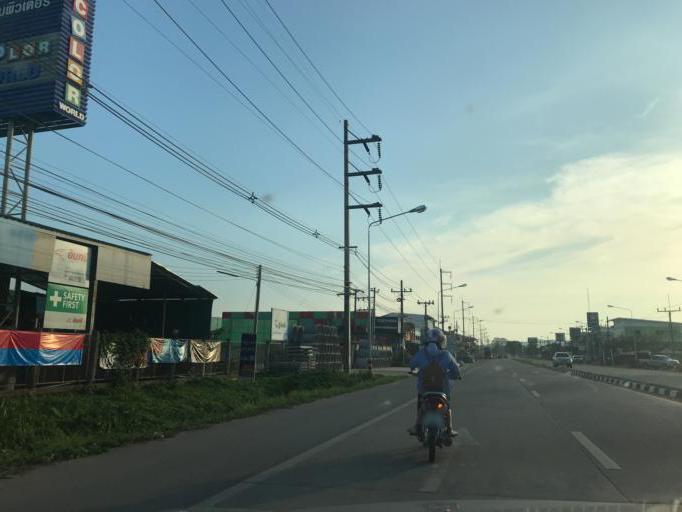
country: TH
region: Phayao
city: Chiang Kham
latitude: 19.5174
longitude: 100.2953
